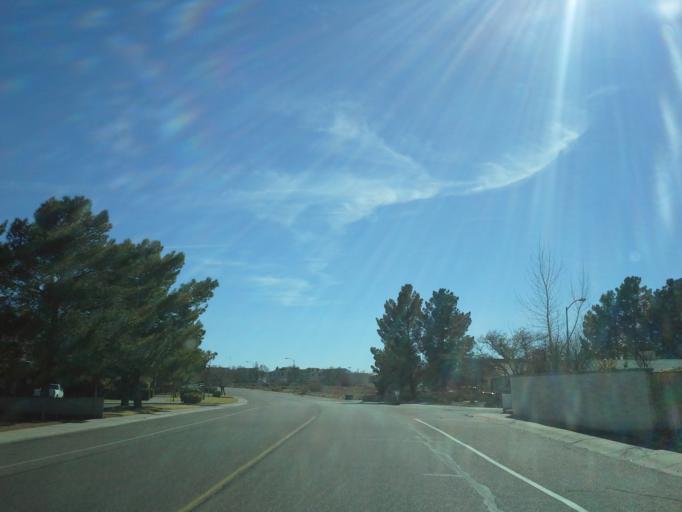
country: US
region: Arizona
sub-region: Coconino County
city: Page
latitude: 36.9285
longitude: -111.4607
